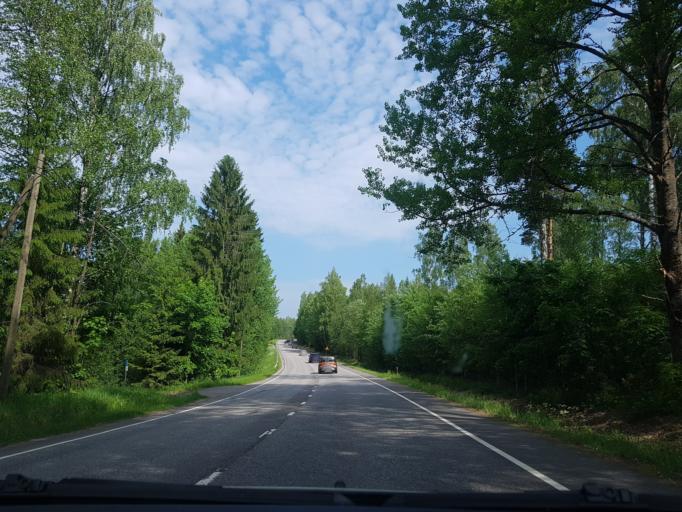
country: FI
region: Uusimaa
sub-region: Helsinki
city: Vihti
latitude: 60.2838
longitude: 24.4085
